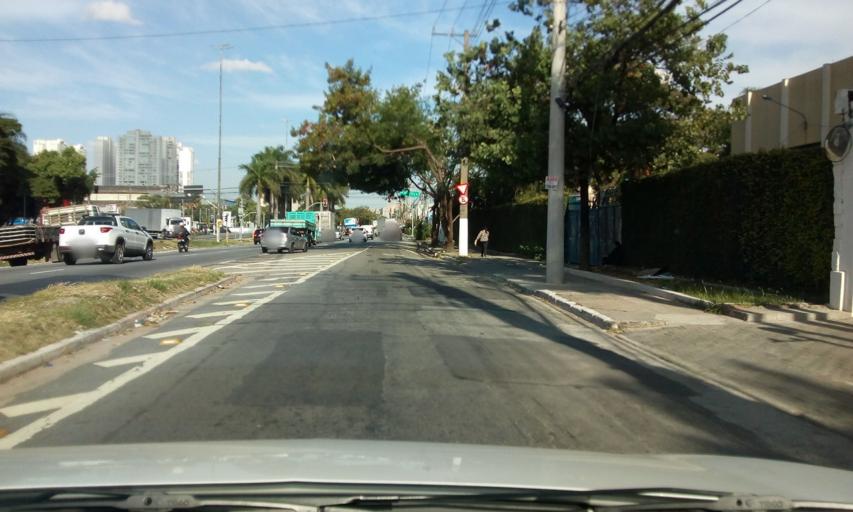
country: BR
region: Sao Paulo
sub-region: Osasco
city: Osasco
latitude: -23.5287
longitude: -46.7394
